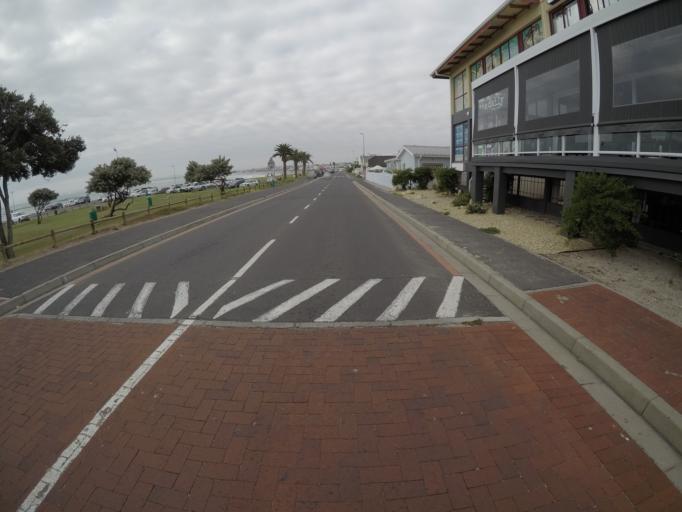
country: ZA
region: Western Cape
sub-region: City of Cape Town
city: Sunset Beach
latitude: -33.7291
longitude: 18.4393
